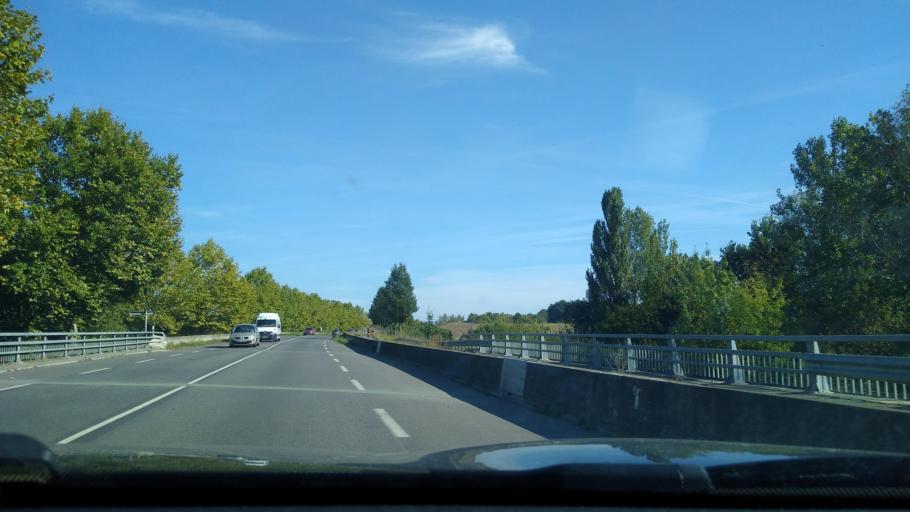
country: FR
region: Midi-Pyrenees
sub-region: Departement de la Haute-Garonne
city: Cornebarrieu
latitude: 43.6609
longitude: 1.3284
